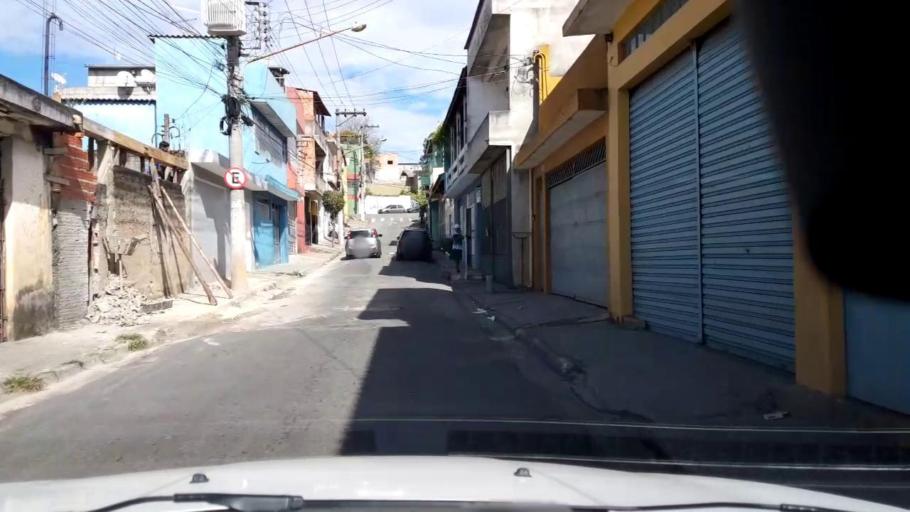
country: BR
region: Sao Paulo
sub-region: Ferraz De Vasconcelos
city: Ferraz de Vasconcelos
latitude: -23.5311
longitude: -46.3922
